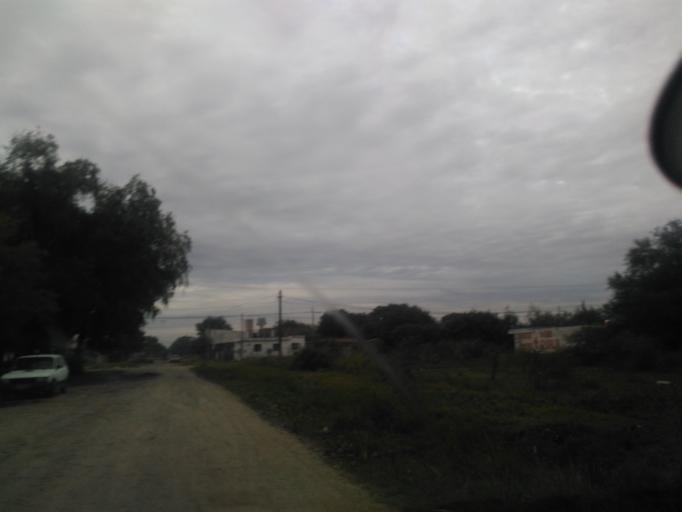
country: AR
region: Chaco
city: Resistencia
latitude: -27.4716
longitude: -59.0110
